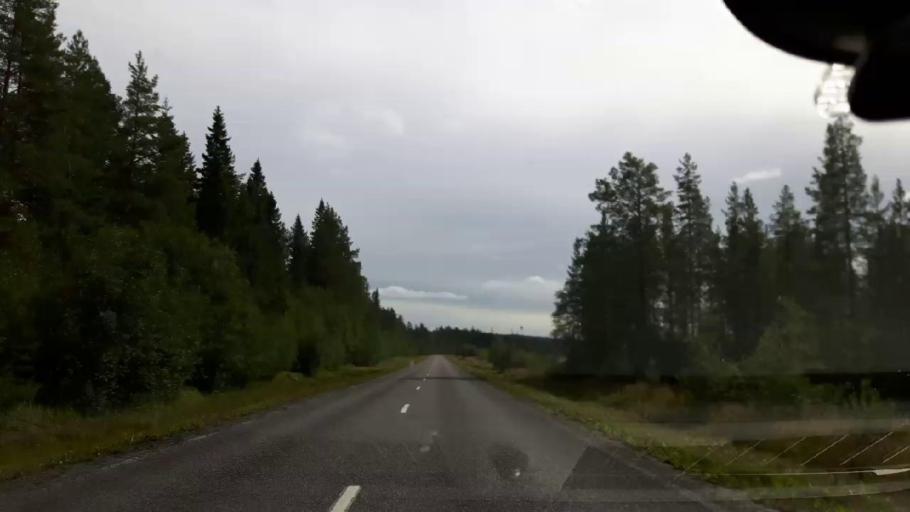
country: SE
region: Jaemtland
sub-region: Ragunda Kommun
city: Hammarstrand
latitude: 63.1305
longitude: 15.8855
